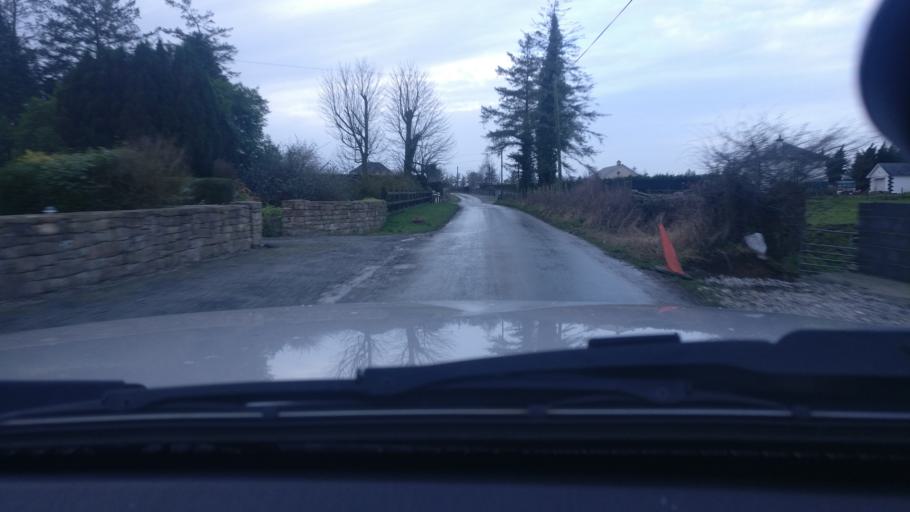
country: IE
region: Connaught
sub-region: County Galway
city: Loughrea
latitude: 53.1640
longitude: -8.5411
